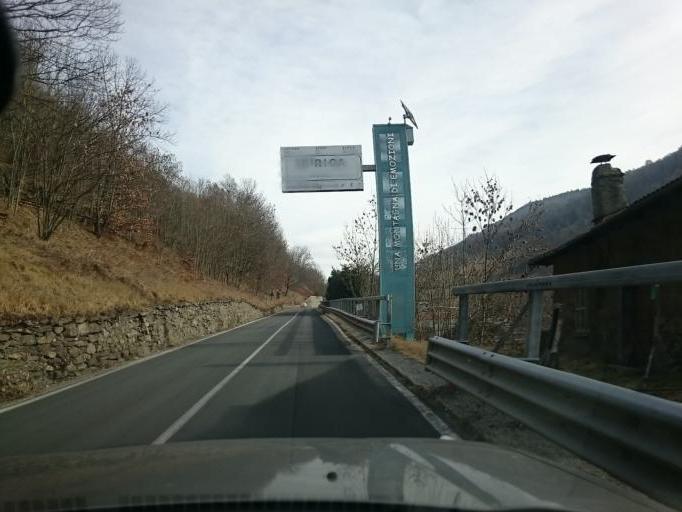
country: IT
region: Lombardy
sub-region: Provincia di Sondrio
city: Aprica
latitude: 46.1495
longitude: 10.1297
